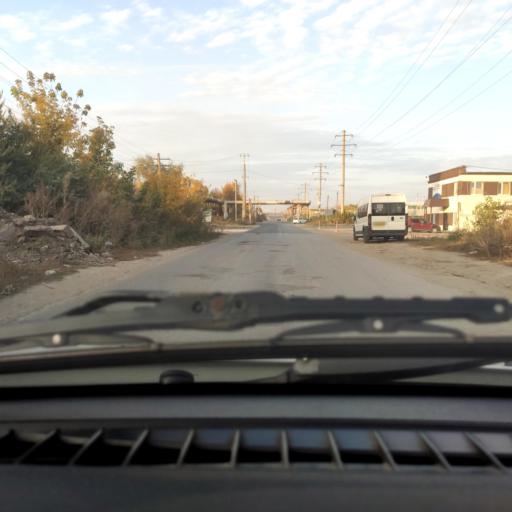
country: RU
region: Samara
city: Tol'yatti
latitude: 53.5298
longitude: 49.4619
